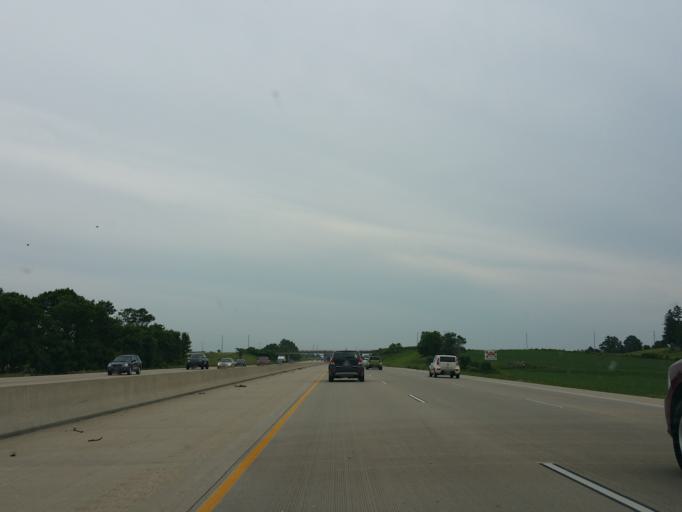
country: US
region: Wisconsin
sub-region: Columbia County
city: Poynette
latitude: 43.3000
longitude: -89.4240
